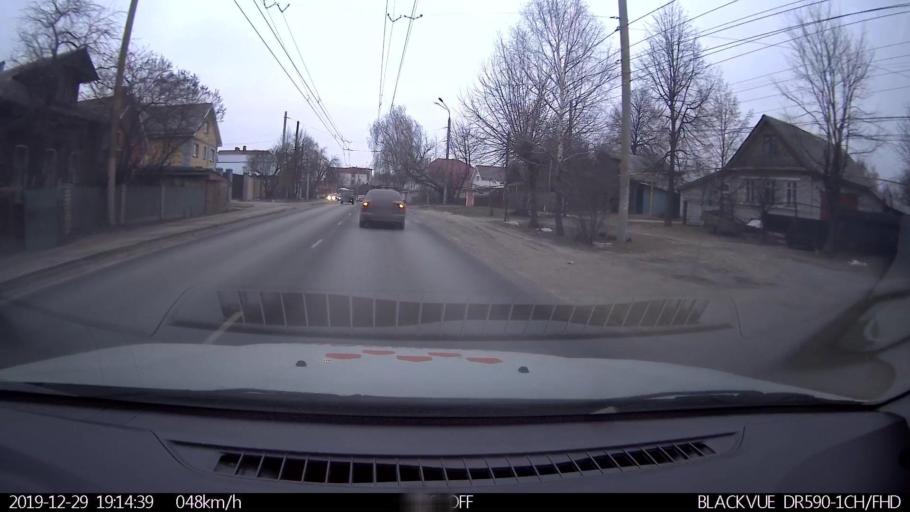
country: RU
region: Nizjnij Novgorod
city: Neklyudovo
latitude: 56.3688
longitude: 43.8446
